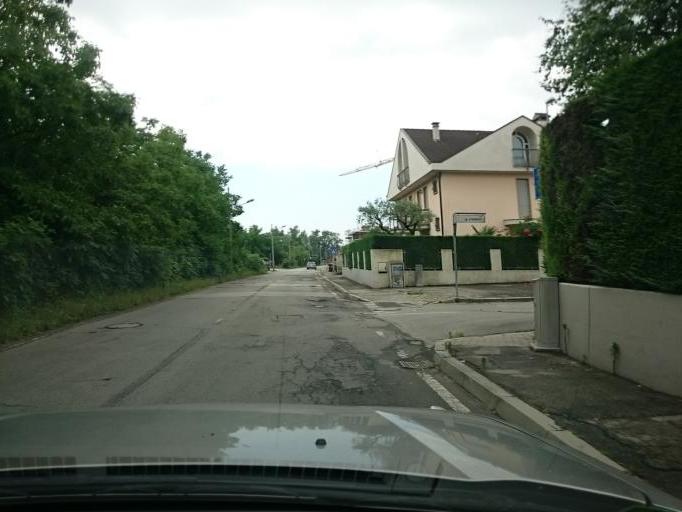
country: IT
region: Veneto
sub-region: Provincia di Padova
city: Padova
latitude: 45.3807
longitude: 11.8785
